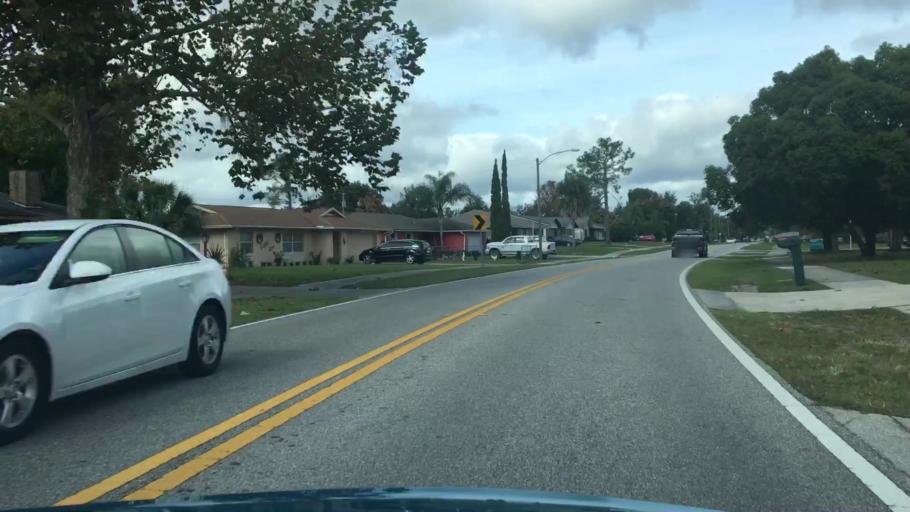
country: US
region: Florida
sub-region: Volusia County
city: Deltona
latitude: 28.8863
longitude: -81.2434
